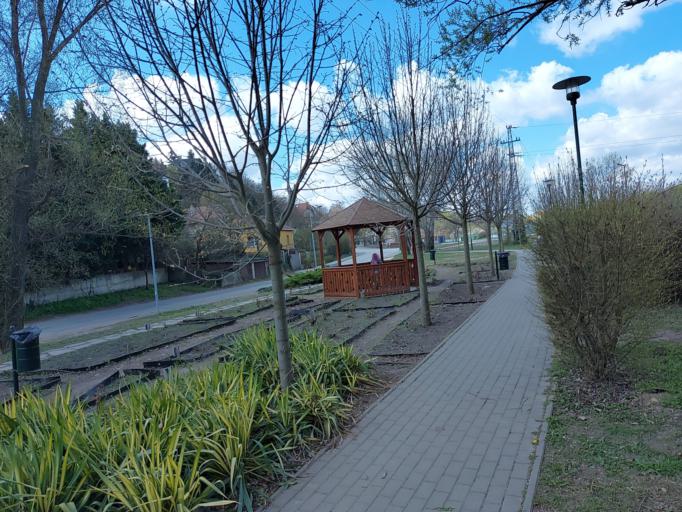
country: HU
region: Pest
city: Budaors
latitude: 47.4399
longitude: 18.9675
